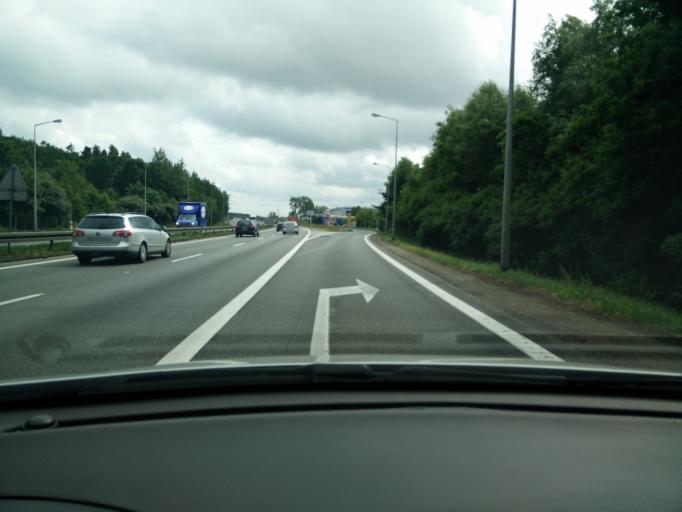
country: PL
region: Pomeranian Voivodeship
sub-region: Gdynia
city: Wielki Kack
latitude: 54.4369
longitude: 18.4879
